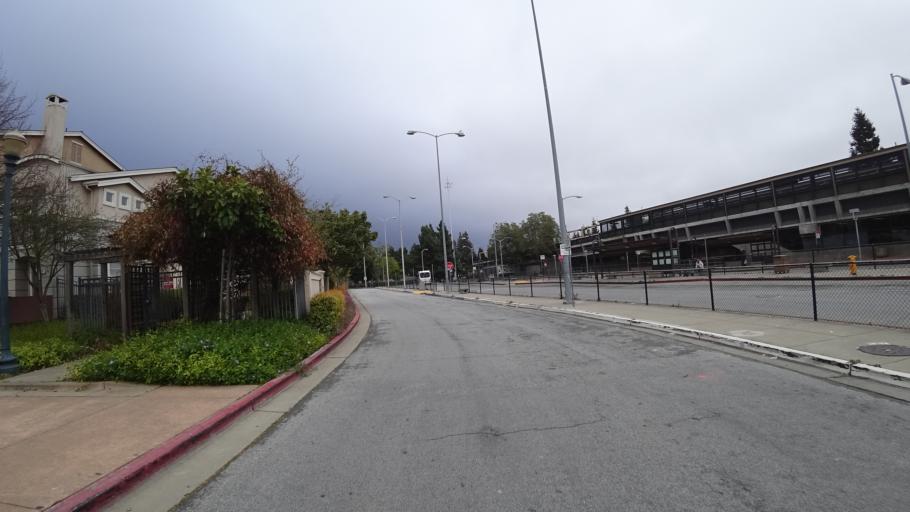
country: US
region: California
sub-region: Alameda County
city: Hayward
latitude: 37.6701
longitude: -122.0867
